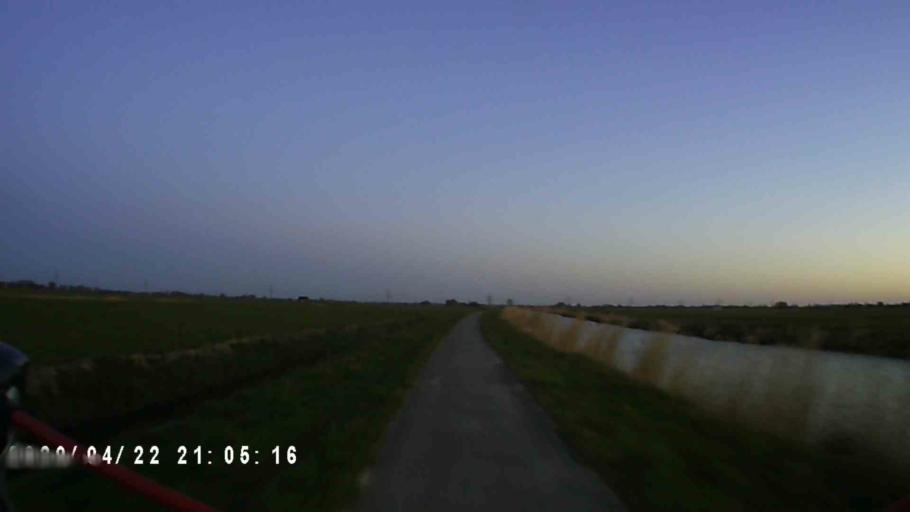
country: NL
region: Groningen
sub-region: Gemeente Winsum
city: Winsum
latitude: 53.3194
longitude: 6.5624
